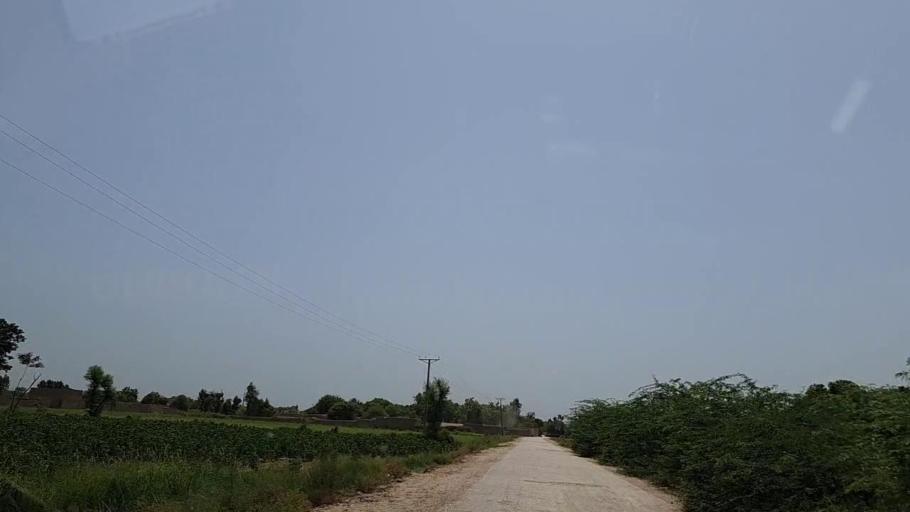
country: PK
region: Sindh
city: Tharu Shah
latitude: 26.9425
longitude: 68.1069
